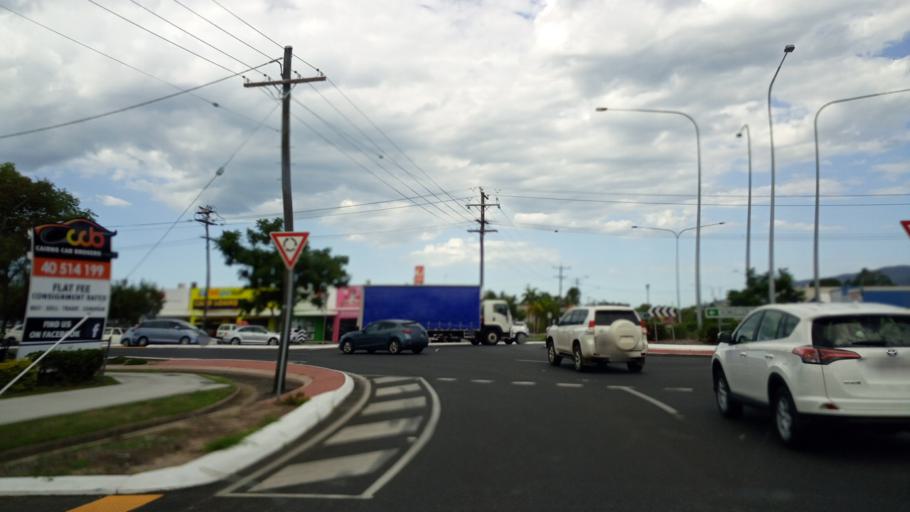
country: AU
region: Queensland
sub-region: Cairns
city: Cairns
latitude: -16.9335
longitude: 145.7606
